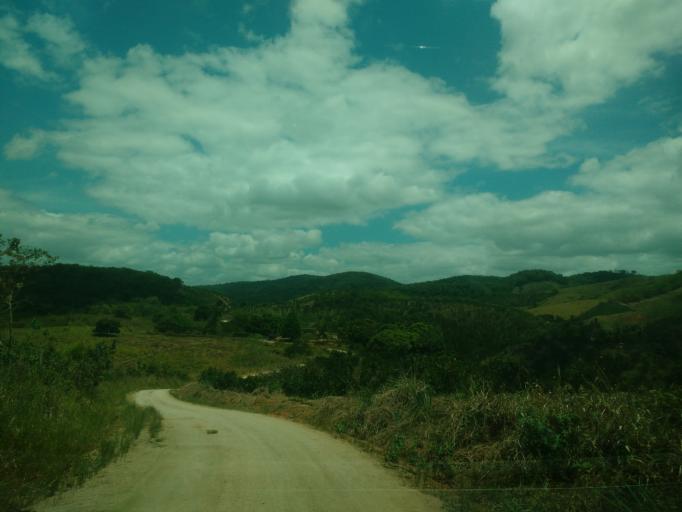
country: BR
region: Alagoas
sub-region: Santana Do Mundau
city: Santana do Mundau
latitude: -9.1566
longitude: -36.1669
